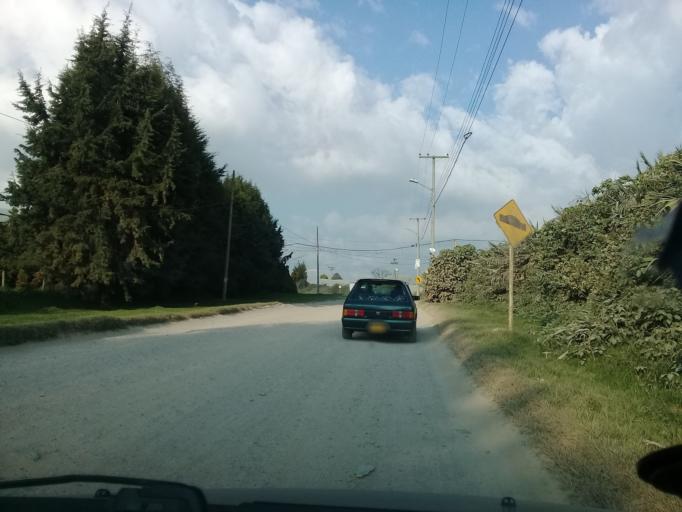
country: CO
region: Cundinamarca
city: Funza
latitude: 4.7502
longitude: -74.2256
